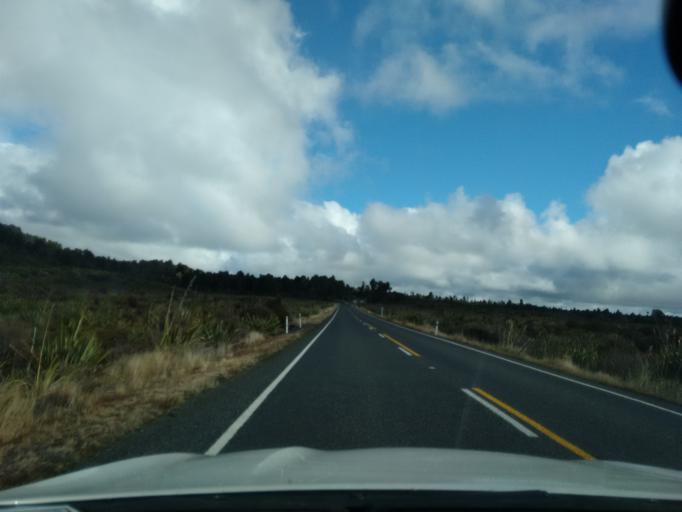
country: NZ
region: Manawatu-Wanganui
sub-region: Ruapehu District
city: Waiouru
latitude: -39.2288
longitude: 175.3953
